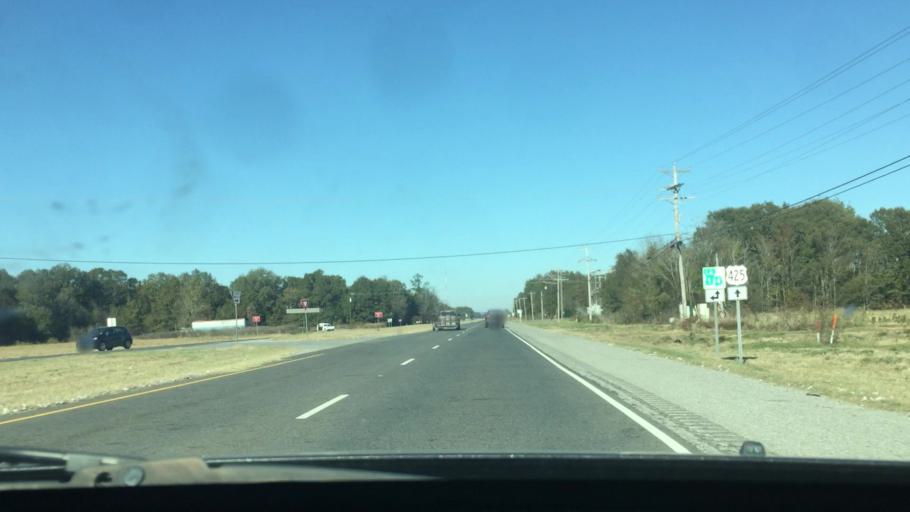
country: US
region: Louisiana
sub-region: Richland Parish
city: Rayville
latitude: 32.4054
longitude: -91.7675
